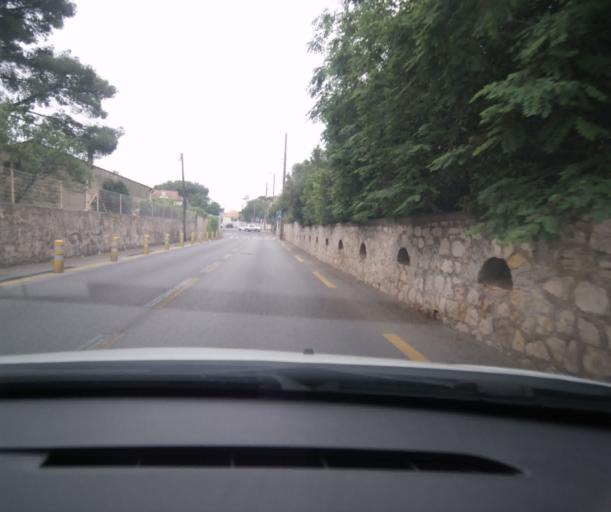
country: FR
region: Provence-Alpes-Cote d'Azur
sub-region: Departement du Var
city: La Valette-du-Var
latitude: 43.1381
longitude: 5.9781
